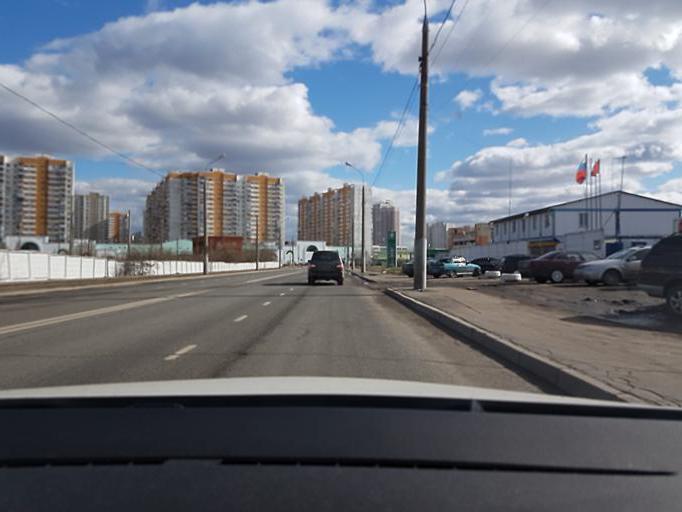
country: RU
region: Moskovskaya
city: Pavshino
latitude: 55.8355
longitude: 37.3474
